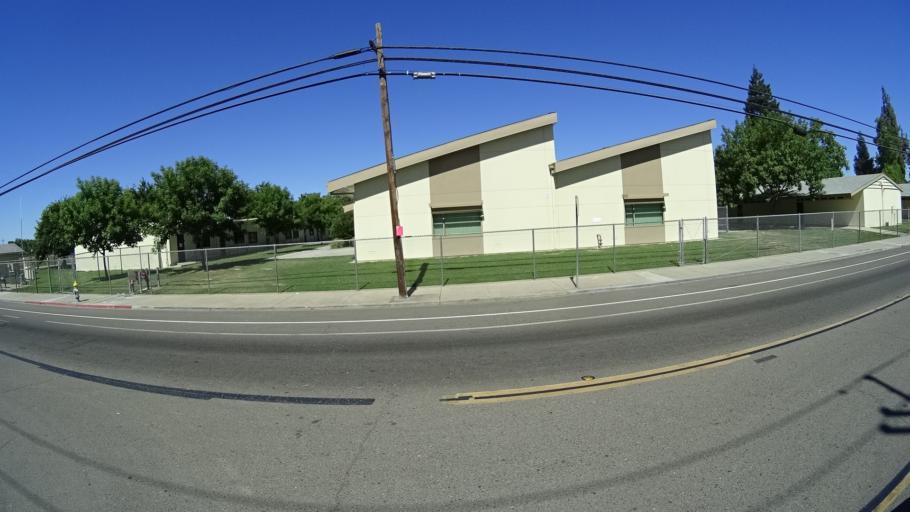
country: US
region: California
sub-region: Fresno County
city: Fresno
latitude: 36.7924
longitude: -119.8355
